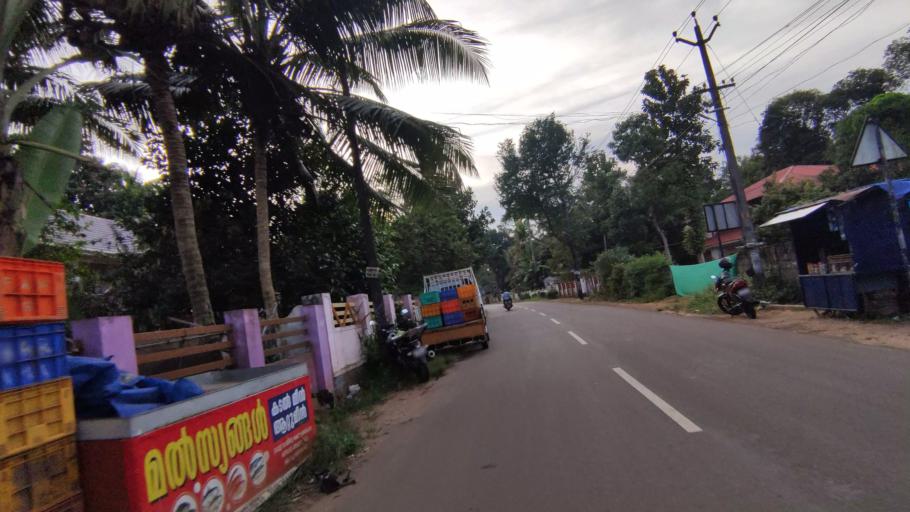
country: IN
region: Kerala
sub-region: Kottayam
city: Kottayam
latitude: 9.6372
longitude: 76.4960
